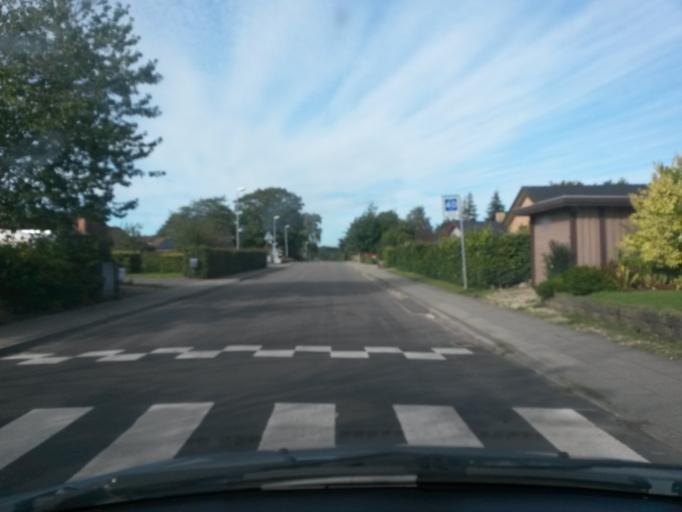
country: DK
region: Central Jutland
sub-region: Silkeborg Kommune
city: Kjellerup
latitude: 56.2844
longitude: 9.4362
